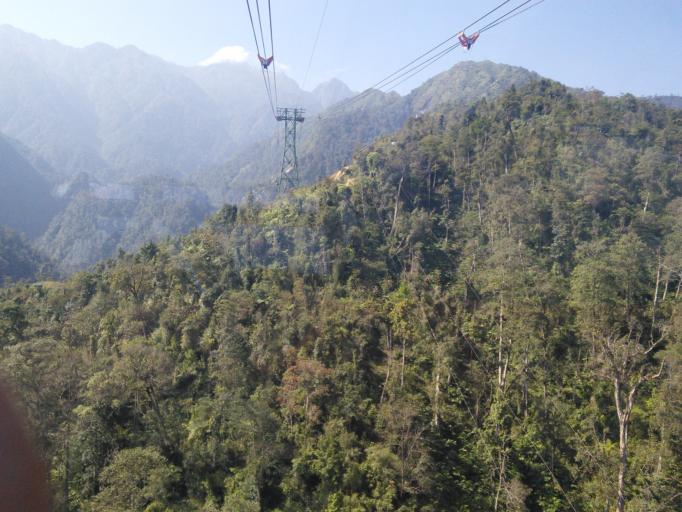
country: VN
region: Lao Cai
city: Sa Pa
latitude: 22.3312
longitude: 103.8146
